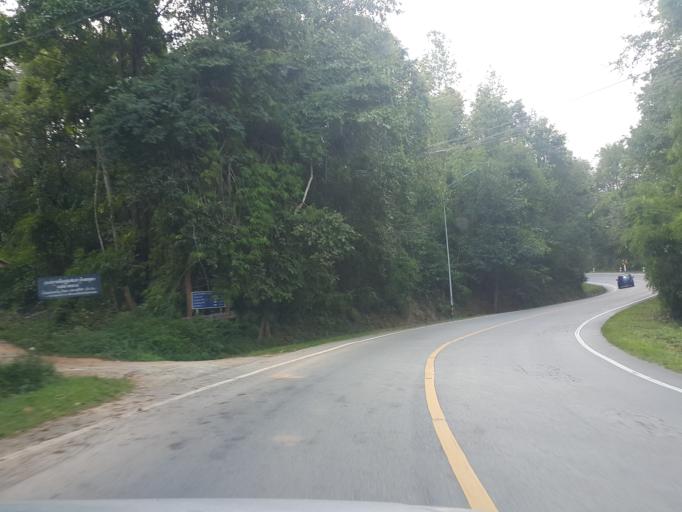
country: TH
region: Chiang Mai
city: Chom Thong
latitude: 18.5300
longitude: 98.6078
